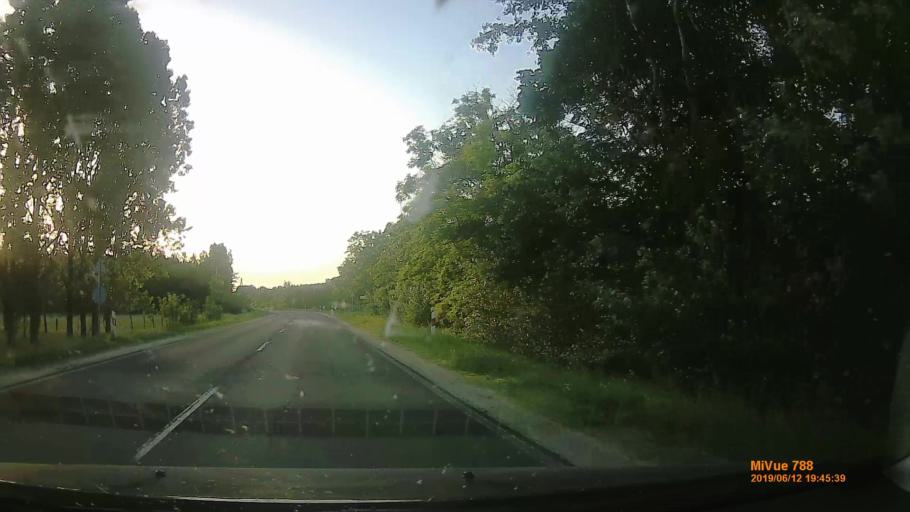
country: HU
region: Pest
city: Taborfalva
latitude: 47.0834
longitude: 19.4865
